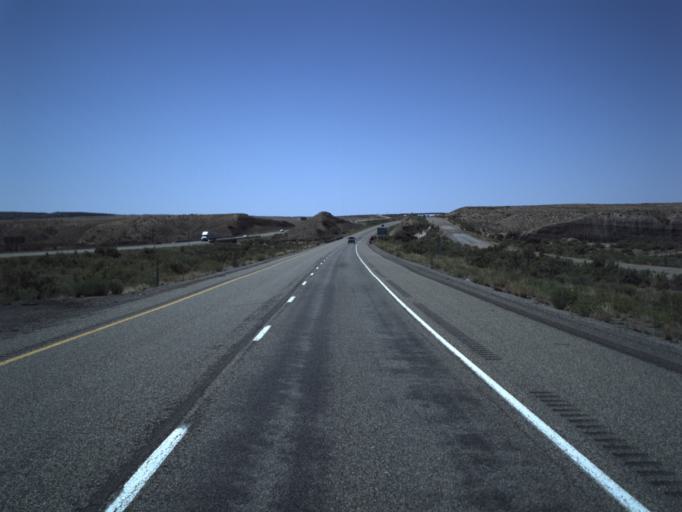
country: US
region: Colorado
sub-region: Mesa County
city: Loma
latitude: 39.1254
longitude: -109.1681
